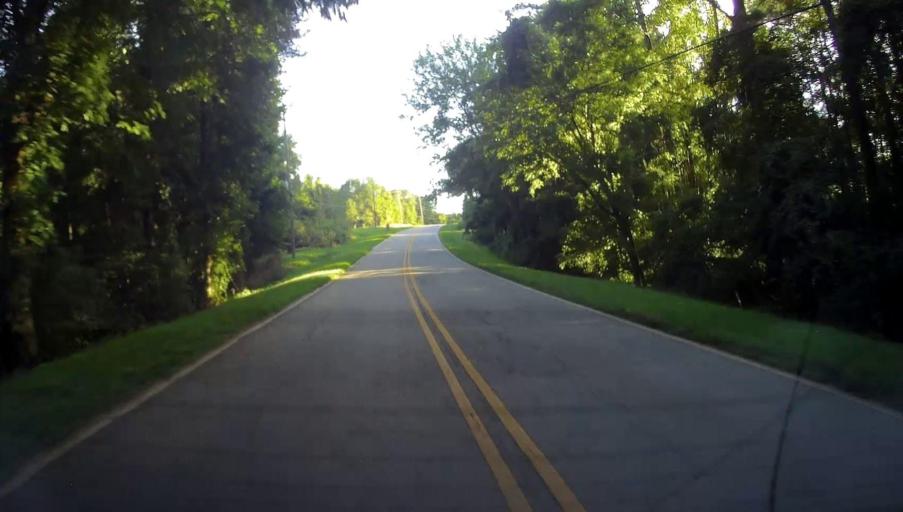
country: US
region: Georgia
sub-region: Muscogee County
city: Columbus
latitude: 32.4295
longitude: -85.0136
